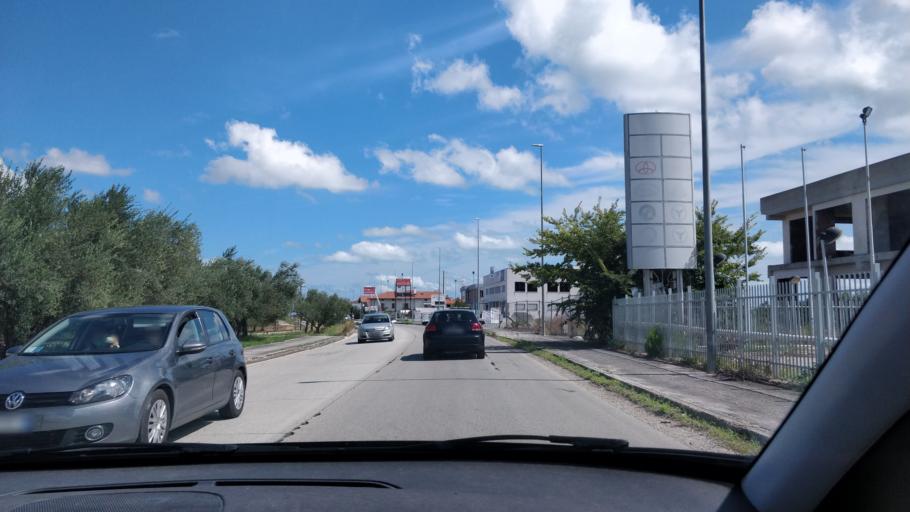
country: IT
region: Abruzzo
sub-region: Provincia di Chieti
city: Treglio
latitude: 42.2537
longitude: 14.4278
